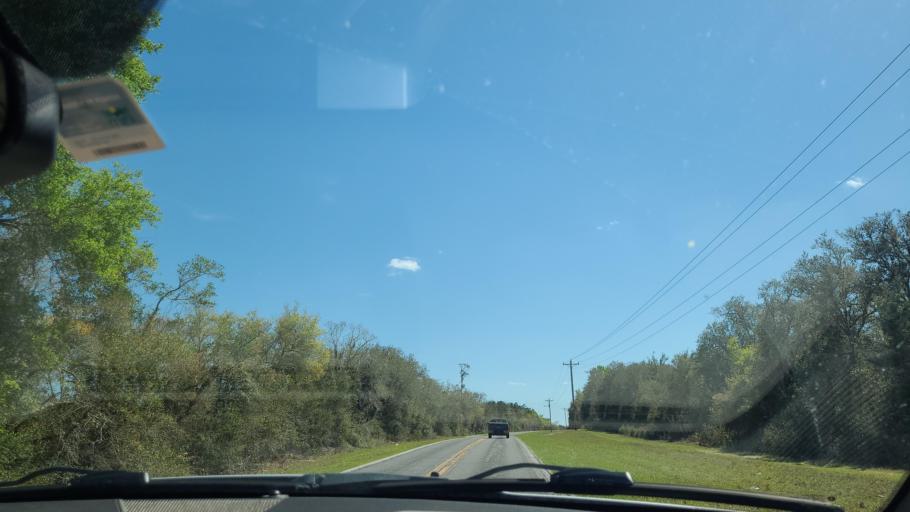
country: US
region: Florida
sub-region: Marion County
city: Citra
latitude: 29.3900
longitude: -81.8893
